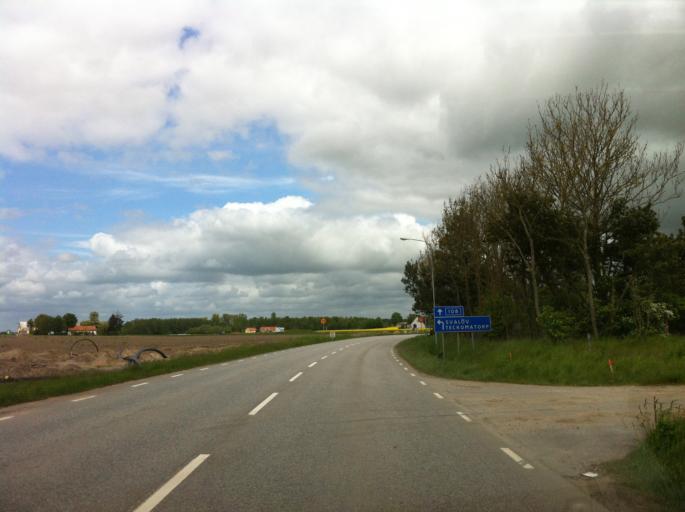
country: SE
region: Skane
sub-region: Svalovs Kommun
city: Teckomatorp
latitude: 55.8402
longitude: 13.1014
